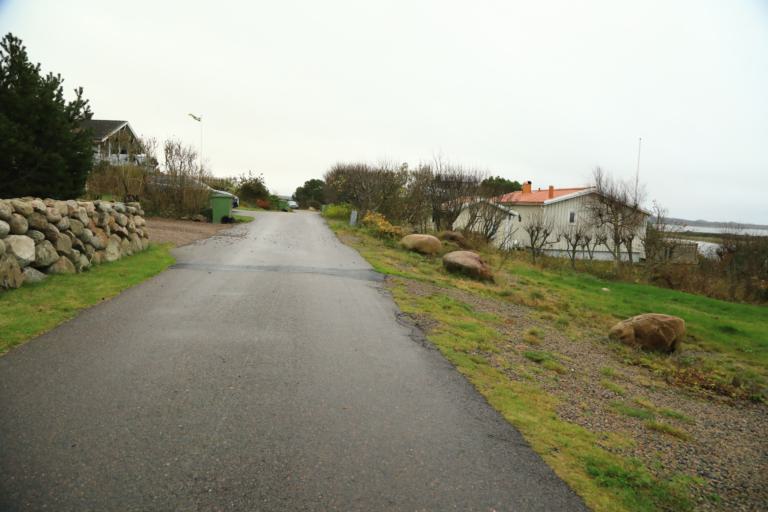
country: SE
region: Halland
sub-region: Varbergs Kommun
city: Varberg
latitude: 57.1686
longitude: 12.2128
